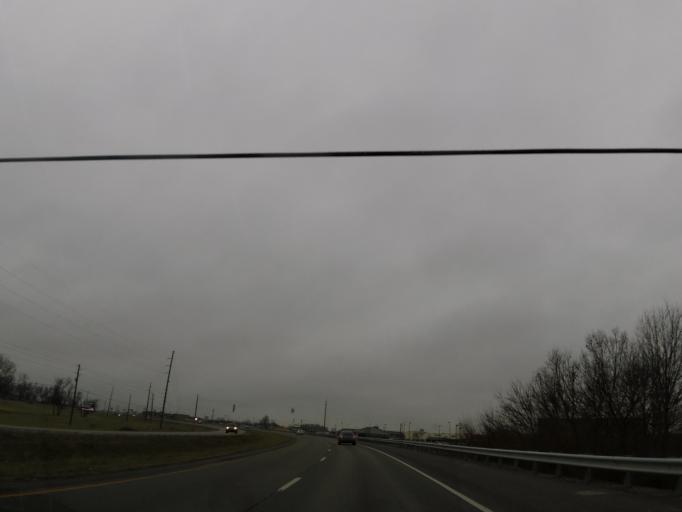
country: US
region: Kentucky
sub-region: Boyle County
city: Danville
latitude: 37.6535
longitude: -84.8020
